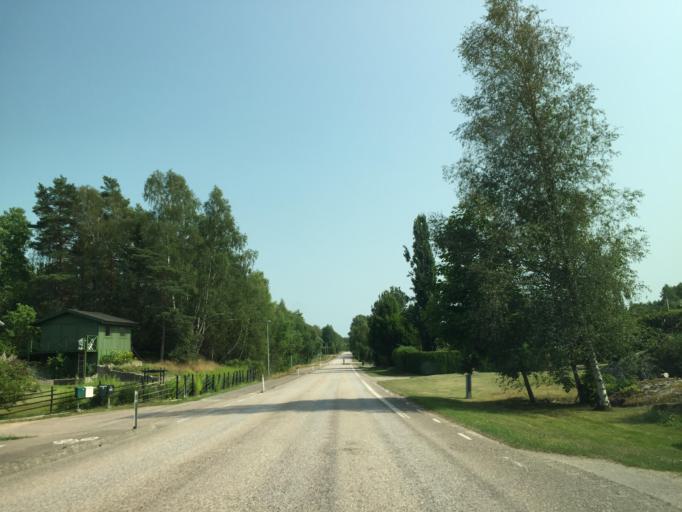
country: SE
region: Vaestra Goetaland
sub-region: Trollhattan
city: Sjuntorp
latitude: 58.3311
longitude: 12.1420
